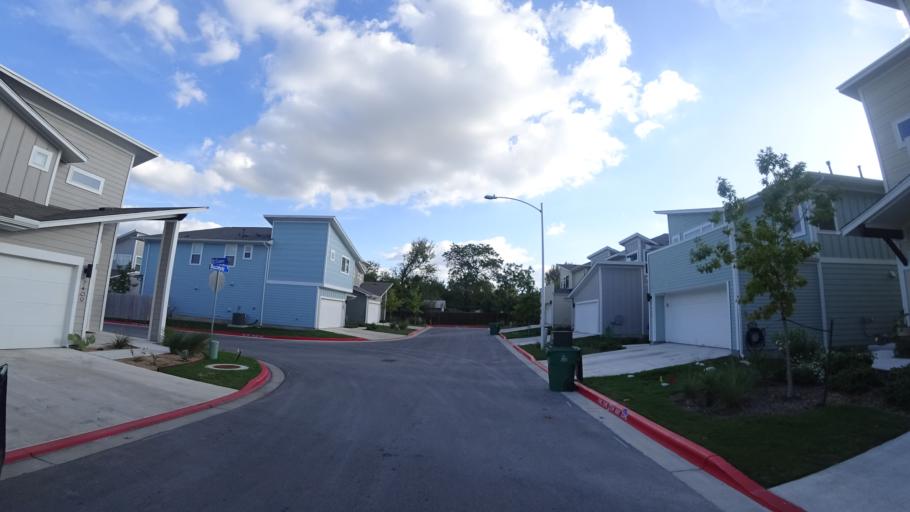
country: US
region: Texas
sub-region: Travis County
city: Onion Creek
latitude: 30.1896
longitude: -97.7937
